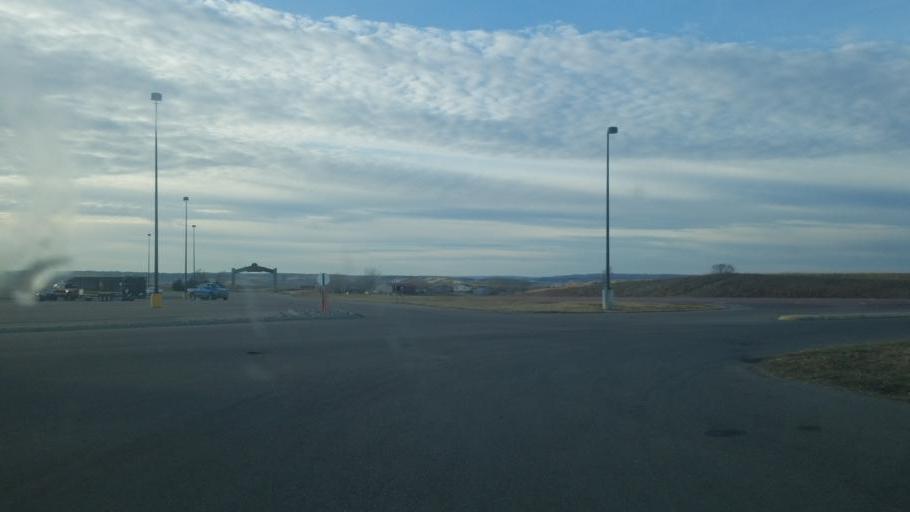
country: US
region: South Dakota
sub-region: Bon Homme County
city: Springfield
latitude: 42.7329
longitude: -97.8874
